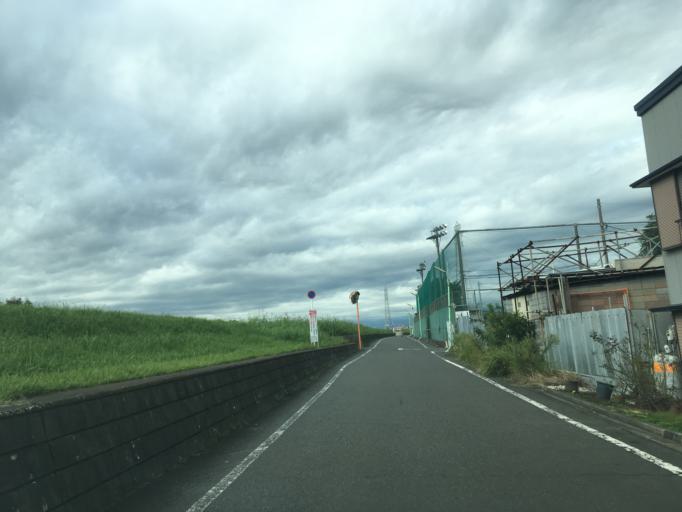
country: JP
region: Tokyo
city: Chofugaoka
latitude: 35.6177
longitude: 139.6065
